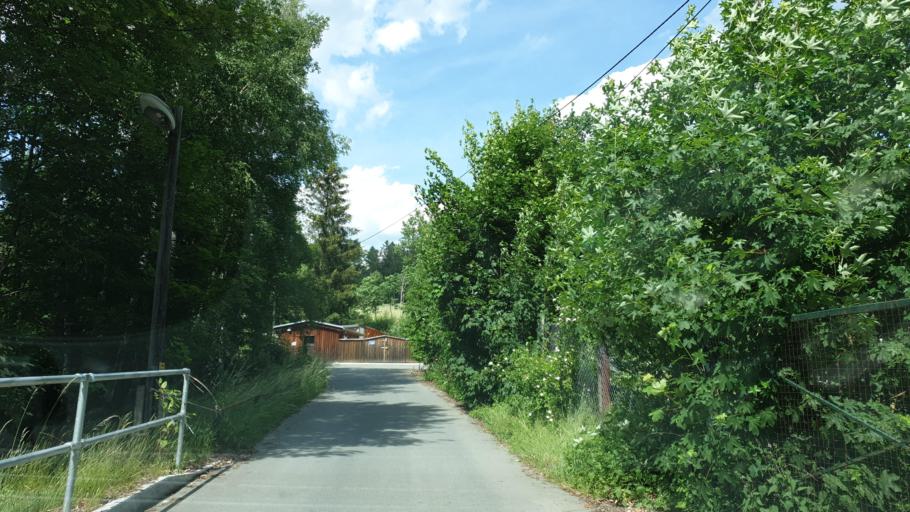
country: DE
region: Saxony
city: Adorf
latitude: 50.3337
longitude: 12.2580
